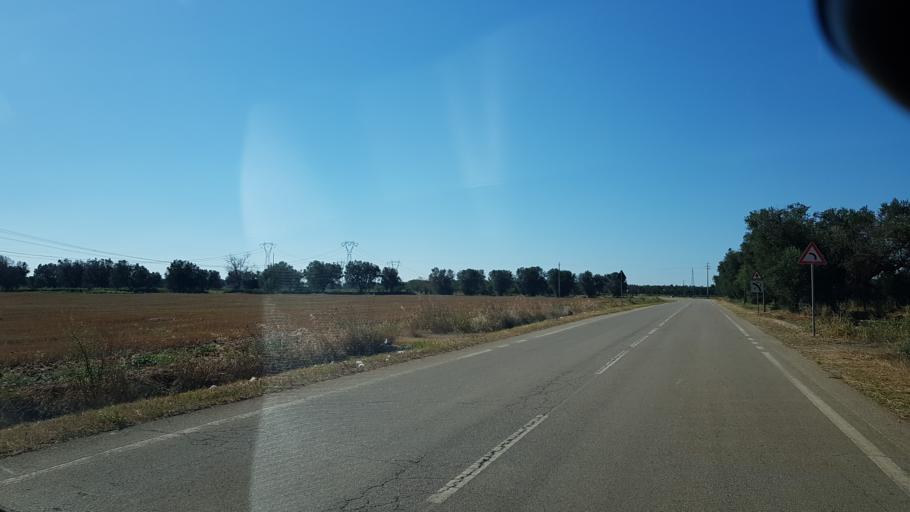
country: IT
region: Apulia
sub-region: Provincia di Brindisi
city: Mesagne
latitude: 40.5538
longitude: 17.8658
